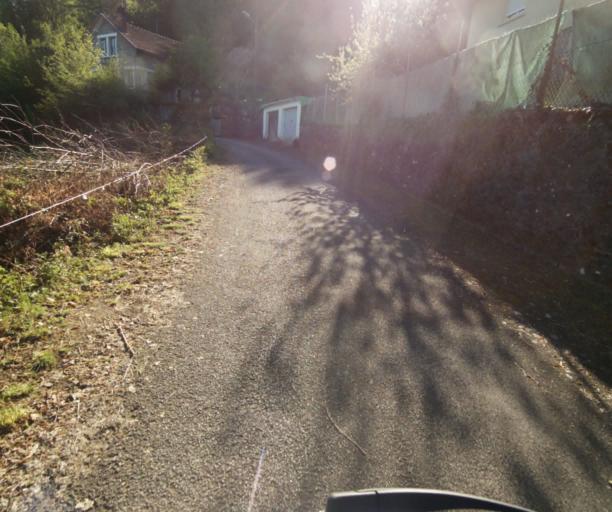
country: FR
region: Limousin
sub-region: Departement de la Correze
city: Tulle
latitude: 45.2712
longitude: 1.7804
